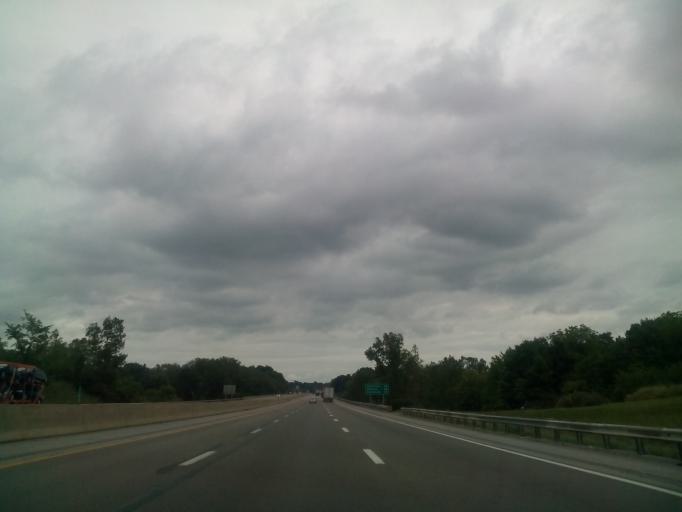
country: US
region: Ohio
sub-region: Erie County
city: Milan
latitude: 41.3242
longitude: -82.5943
